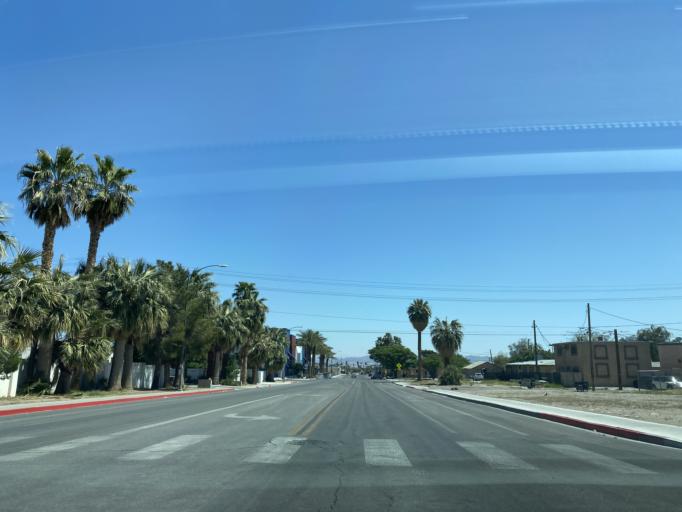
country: US
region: Nevada
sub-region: Clark County
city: Las Vegas
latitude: 36.1657
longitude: -115.1358
